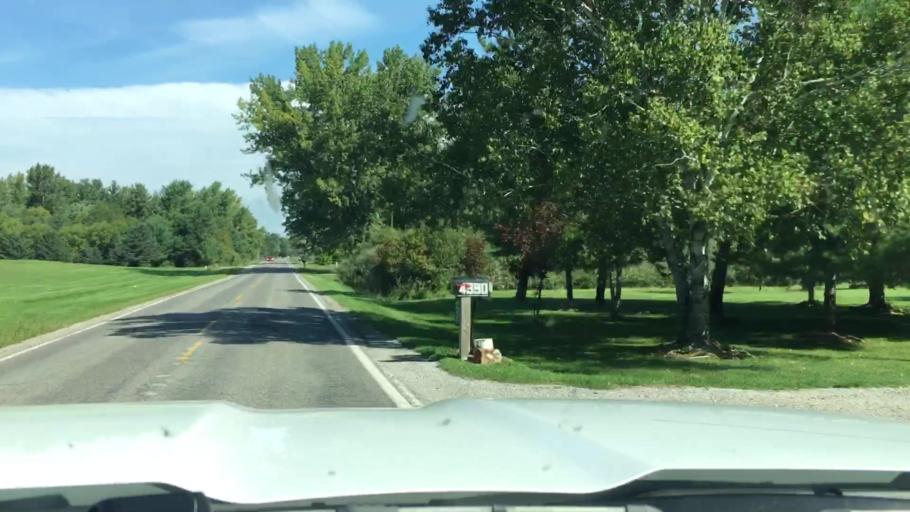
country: US
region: Michigan
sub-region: Saginaw County
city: Hemlock
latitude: 43.4740
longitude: -84.2303
